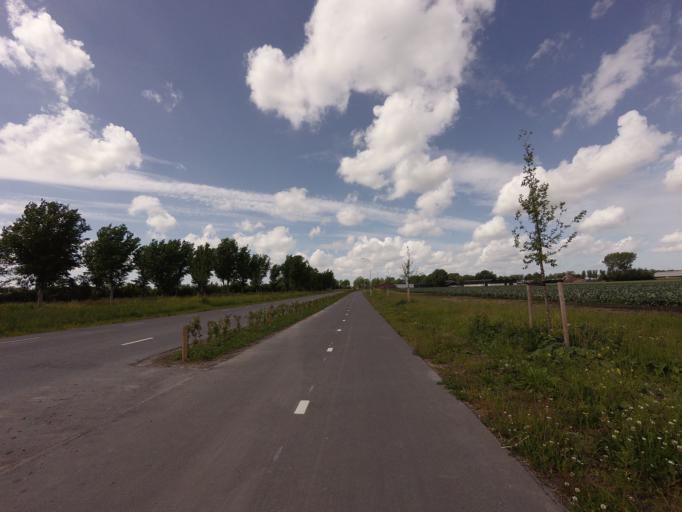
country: NL
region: North Holland
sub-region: Gemeente Hoorn
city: Hoorn
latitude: 52.6831
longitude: 5.0876
